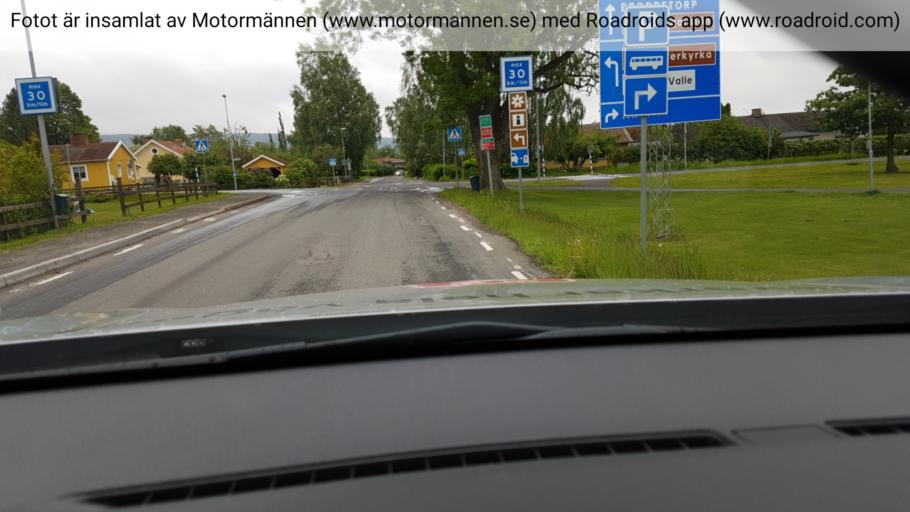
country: SE
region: Vaestra Goetaland
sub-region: Skara Kommun
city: Axvall
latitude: 58.3869
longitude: 13.6492
